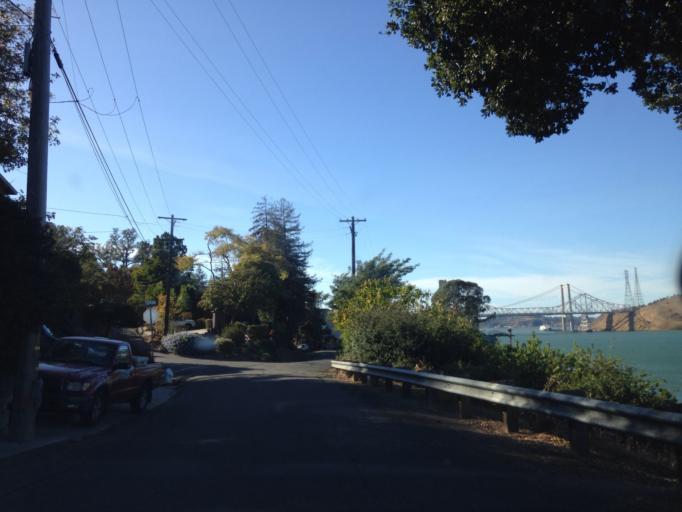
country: US
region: California
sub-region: Contra Costa County
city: Crockett
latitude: 38.0548
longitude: -122.2090
